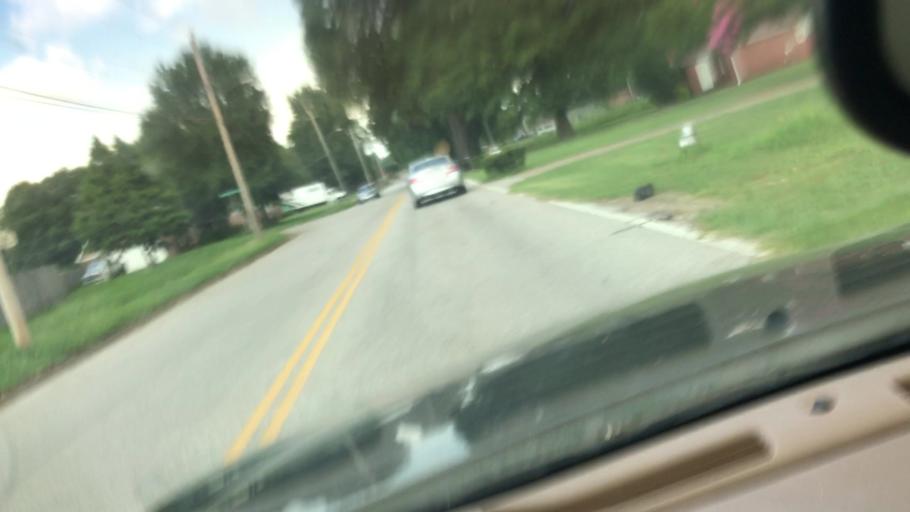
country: US
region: Tennessee
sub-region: Shelby County
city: Bartlett
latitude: 35.1938
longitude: -89.8054
